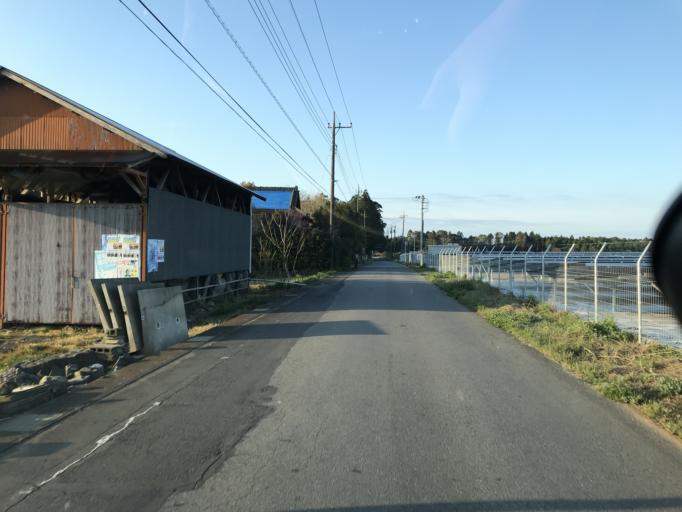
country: JP
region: Chiba
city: Yokaichiba
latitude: 35.7821
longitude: 140.5351
